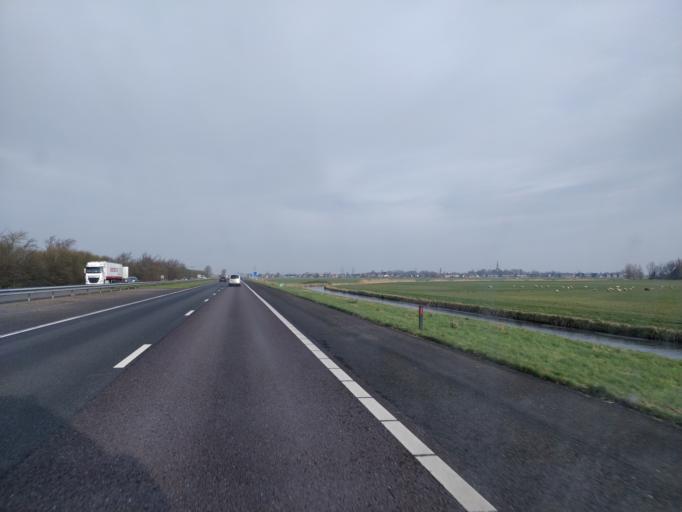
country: NL
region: Friesland
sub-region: Gemeente Leeuwarden
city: Wirdum
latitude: 53.1362
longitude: 5.8003
